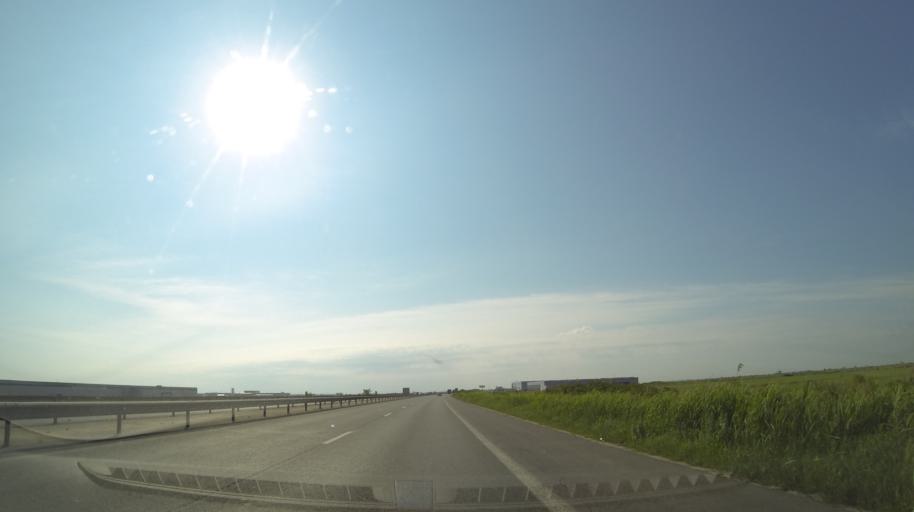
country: RO
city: Oarja Sat
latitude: 44.7966
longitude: 24.9797
